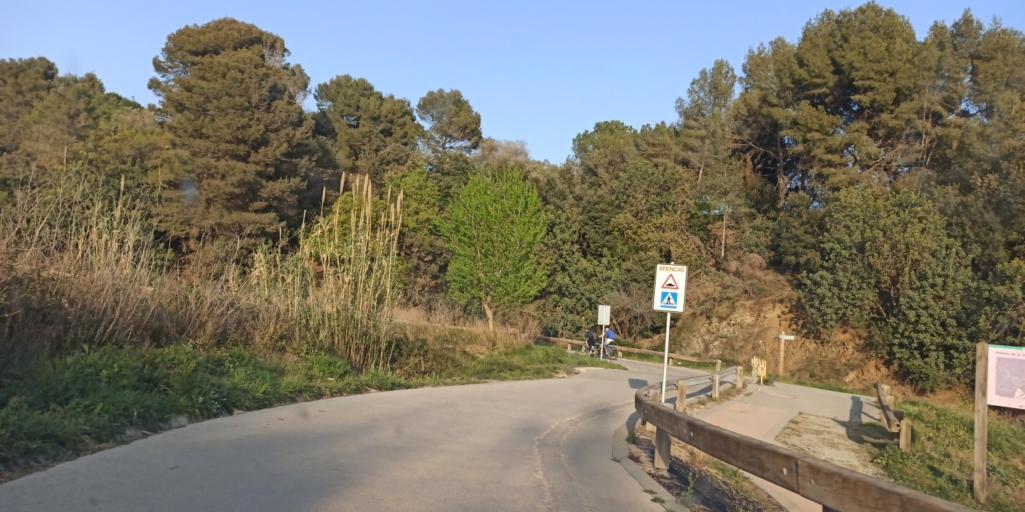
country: ES
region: Catalonia
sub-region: Provincia de Barcelona
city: Sant Just Desvern
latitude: 41.4008
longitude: 2.0871
